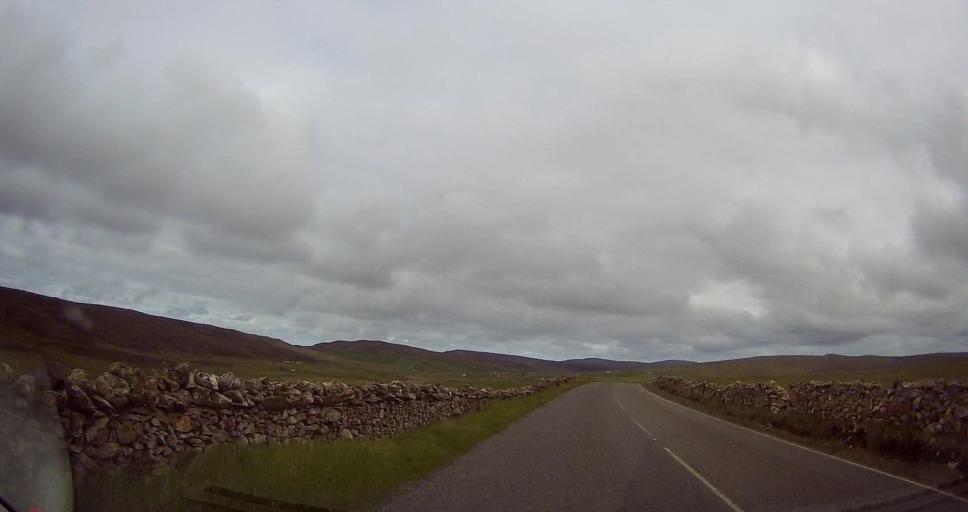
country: GB
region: Scotland
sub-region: Shetland Islands
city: Shetland
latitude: 60.7475
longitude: -0.8851
